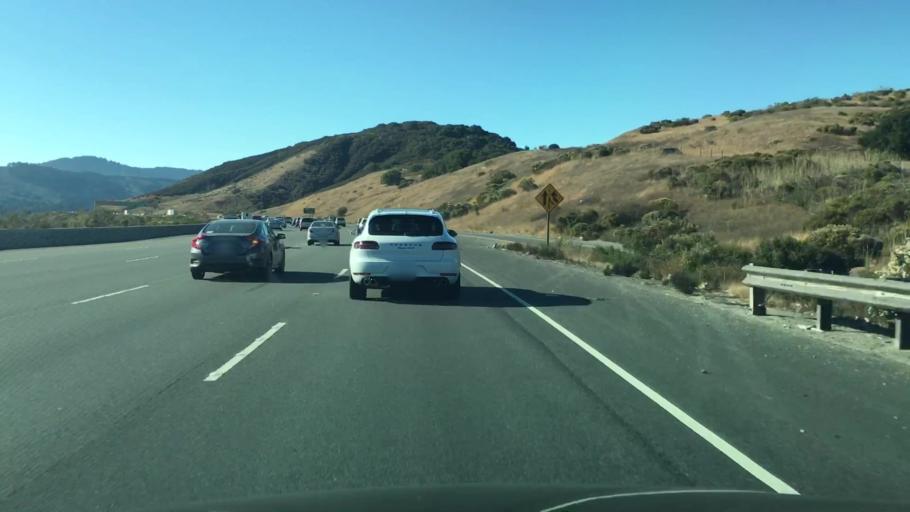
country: US
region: California
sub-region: San Mateo County
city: Highlands-Baywood Park
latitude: 37.4994
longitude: -122.3172
